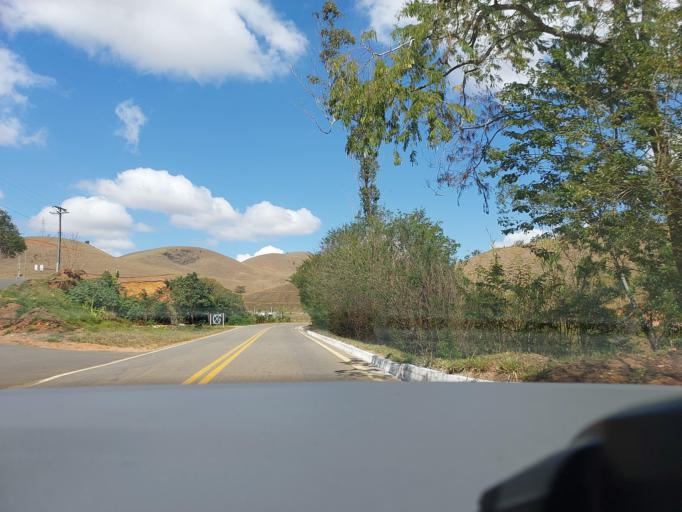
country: BR
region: Minas Gerais
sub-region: Muriae
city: Muriae
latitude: -21.0702
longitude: -42.5068
